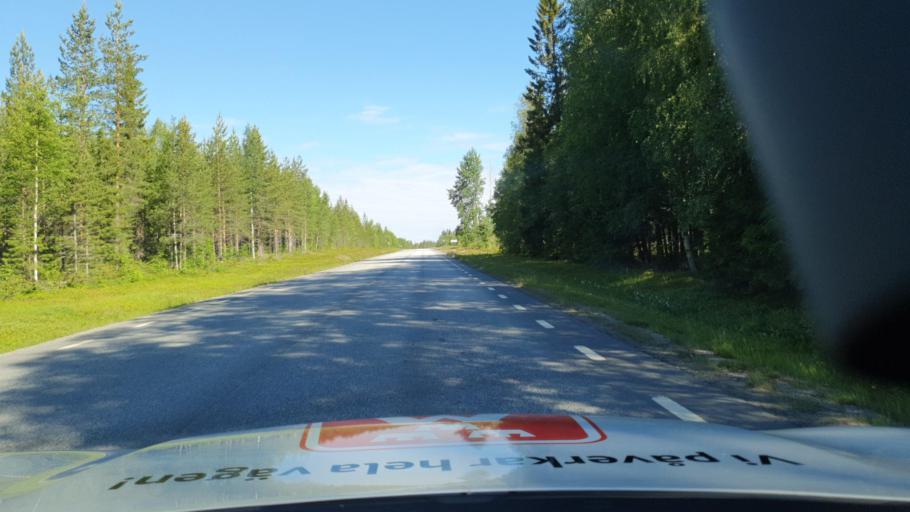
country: SE
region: Vaesterbotten
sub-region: Vannas Kommun
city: Vannasby
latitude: 64.0404
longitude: 20.0066
